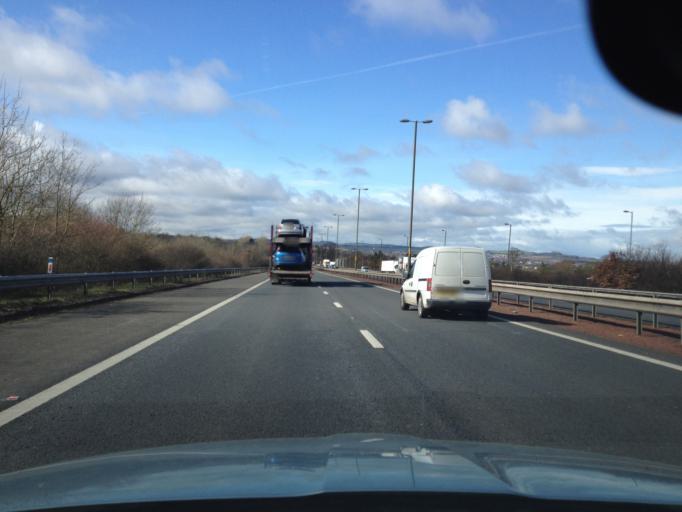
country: GB
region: Scotland
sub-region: Edinburgh
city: Newbridge
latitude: 55.9257
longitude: -3.4097
